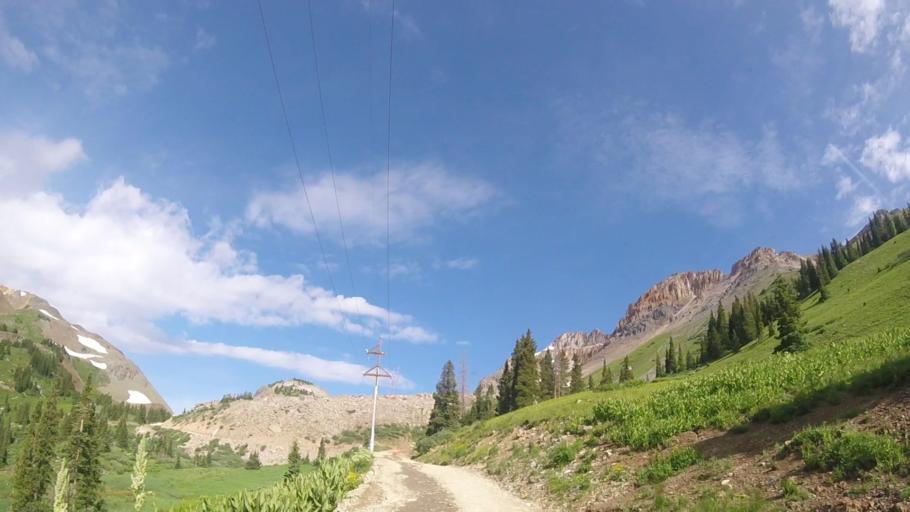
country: US
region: Colorado
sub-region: San Miguel County
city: Telluride
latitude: 37.8504
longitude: -107.7706
